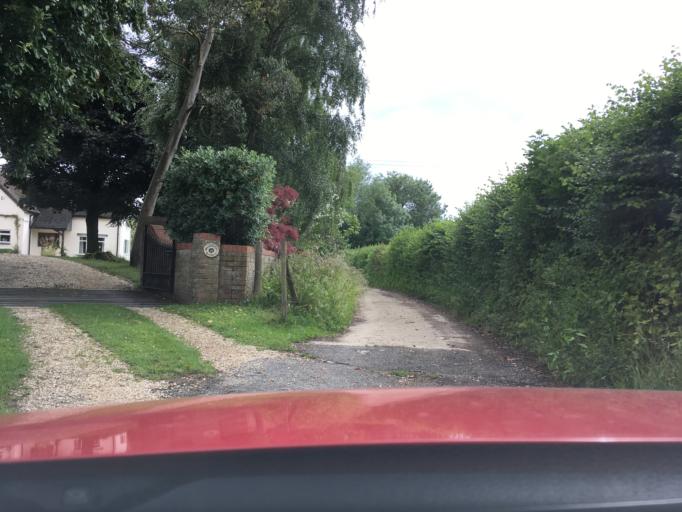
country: GB
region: England
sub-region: Gloucestershire
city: Cinderford
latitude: 51.7989
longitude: -2.4169
